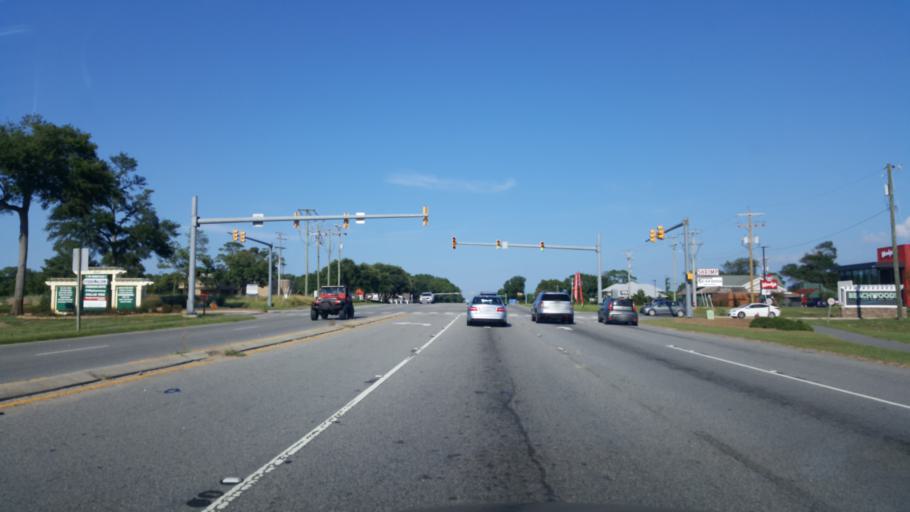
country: US
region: North Carolina
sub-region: Dare County
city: Kitty Hawk
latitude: 36.0981
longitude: -75.7237
